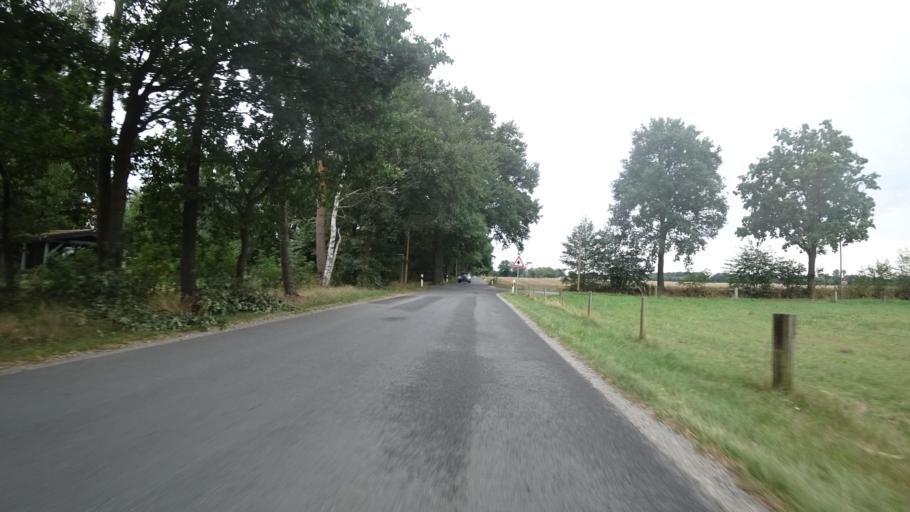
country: DE
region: North Rhine-Westphalia
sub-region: Regierungsbezirk Detmold
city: Rheda-Wiedenbruck
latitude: 51.8769
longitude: 8.2963
